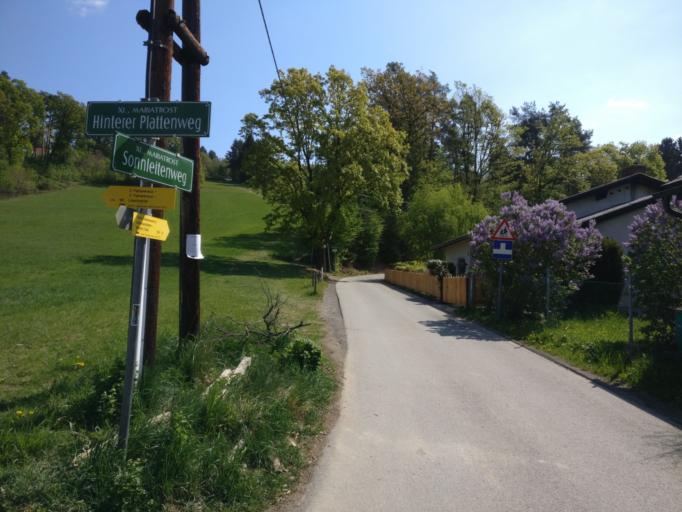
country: AT
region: Styria
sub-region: Graz Stadt
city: Mariatrost
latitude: 47.1093
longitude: 15.4636
